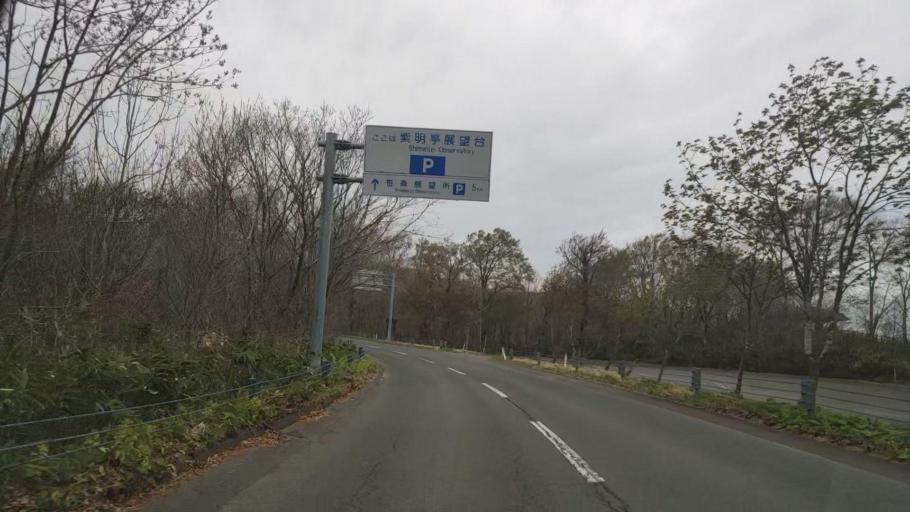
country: JP
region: Akita
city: Hanawa
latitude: 40.4071
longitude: 140.8606
